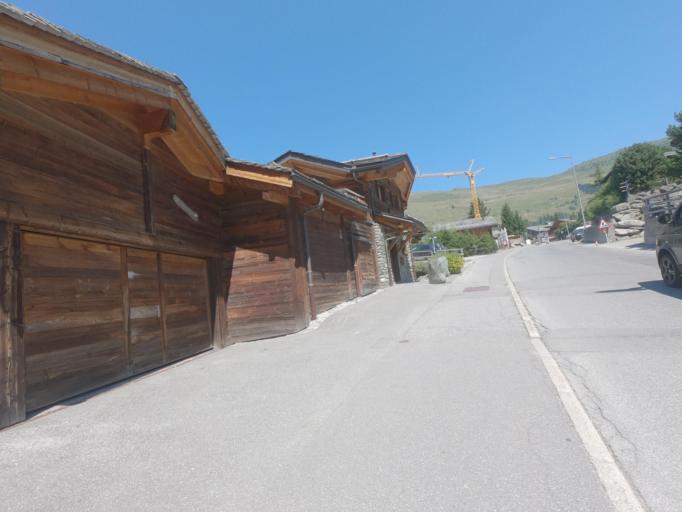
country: CH
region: Valais
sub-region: Entremont District
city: Verbier
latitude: 46.0970
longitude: 7.2324
